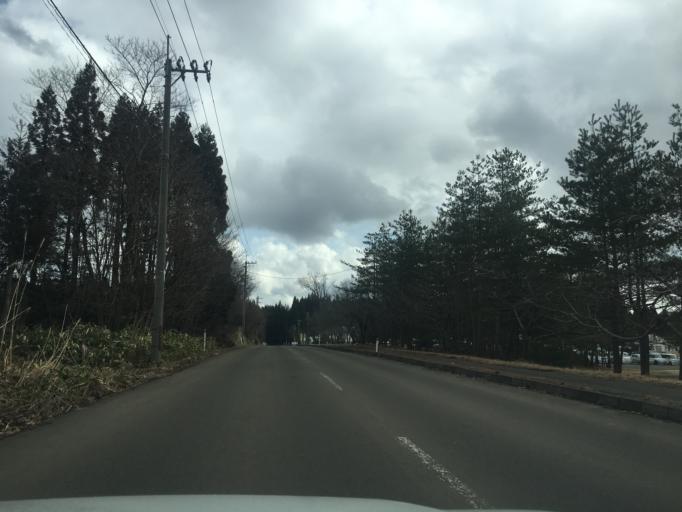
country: JP
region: Akita
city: Takanosu
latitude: 40.1876
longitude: 140.3496
